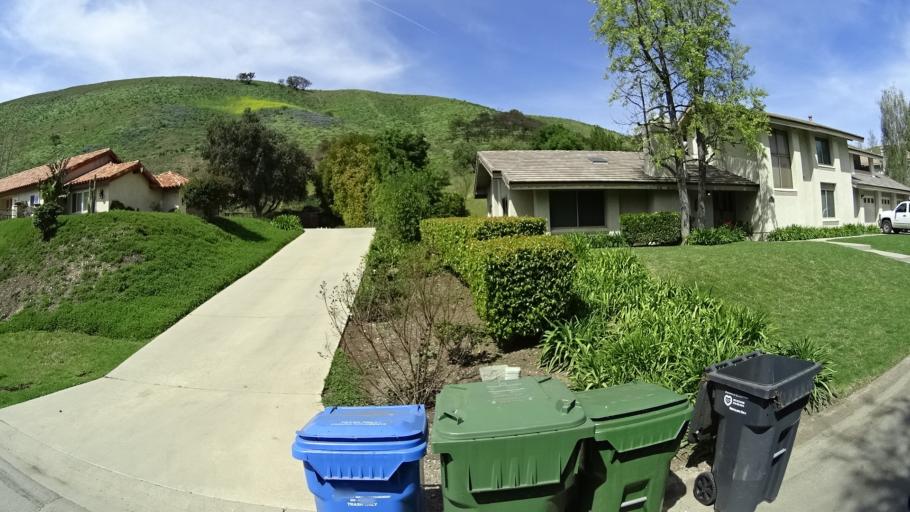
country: US
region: California
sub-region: Ventura County
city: Thousand Oaks
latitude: 34.1826
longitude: -118.8240
